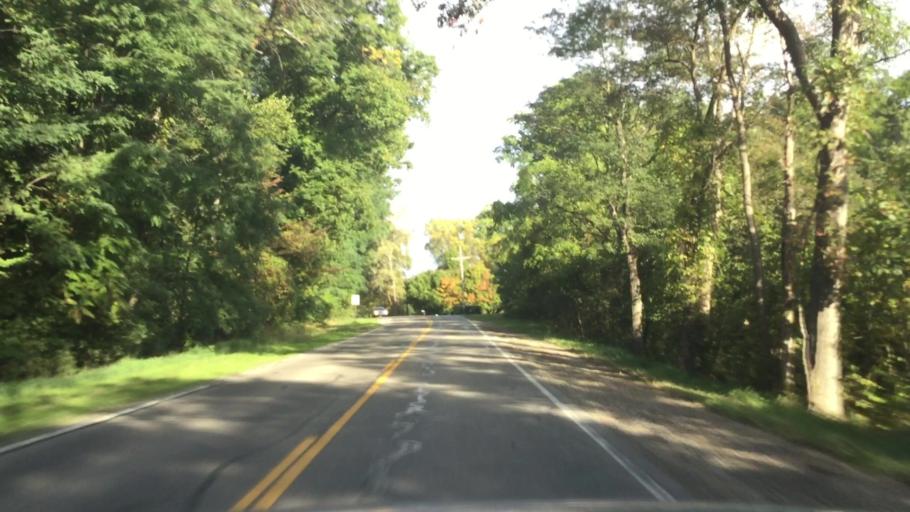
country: US
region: Michigan
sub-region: Livingston County
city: Howell
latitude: 42.5619
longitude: -83.8902
